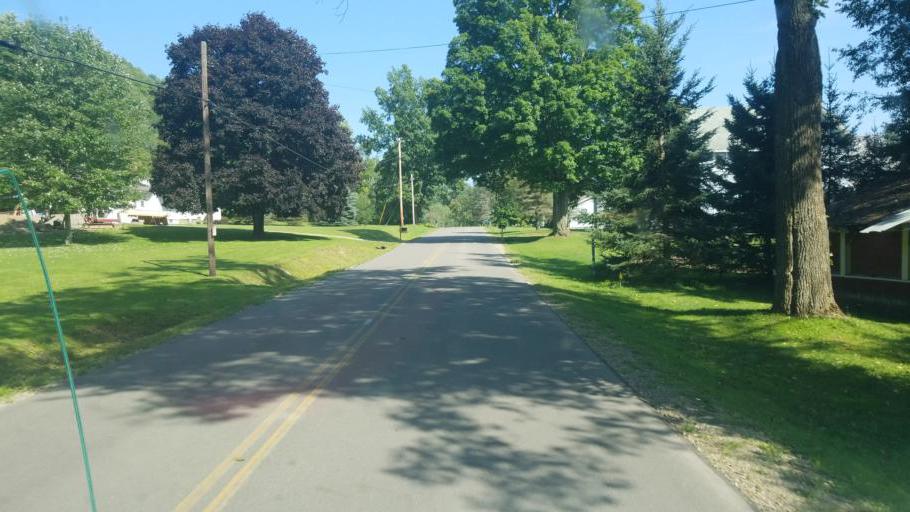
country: US
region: New York
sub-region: Allegany County
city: Bolivar
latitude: 42.0126
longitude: -78.0538
